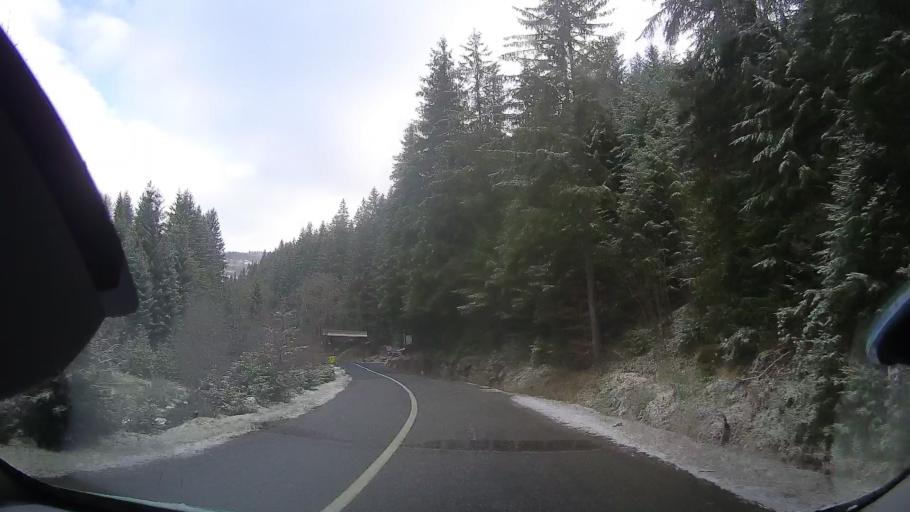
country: RO
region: Alba
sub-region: Comuna Horea
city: Horea
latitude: 46.4905
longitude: 22.9617
